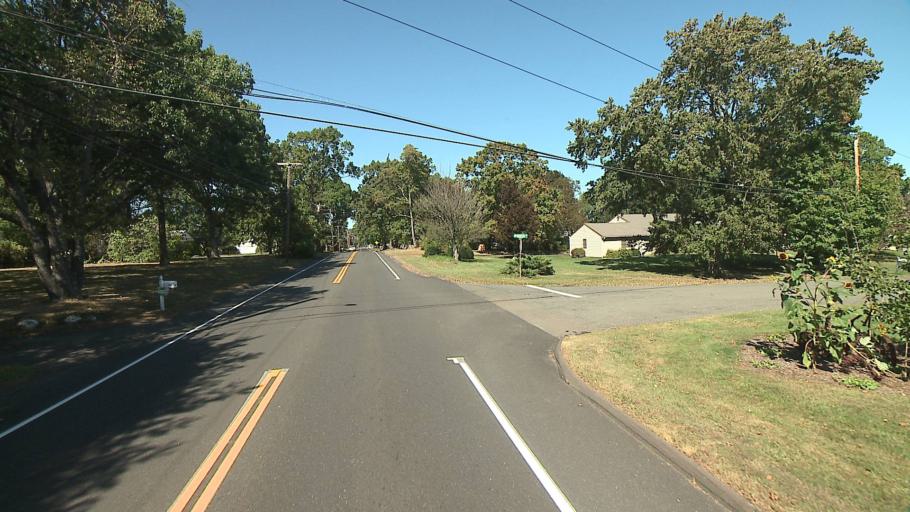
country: US
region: Connecticut
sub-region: New Haven County
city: Orange
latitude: 41.2705
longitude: -73.0204
